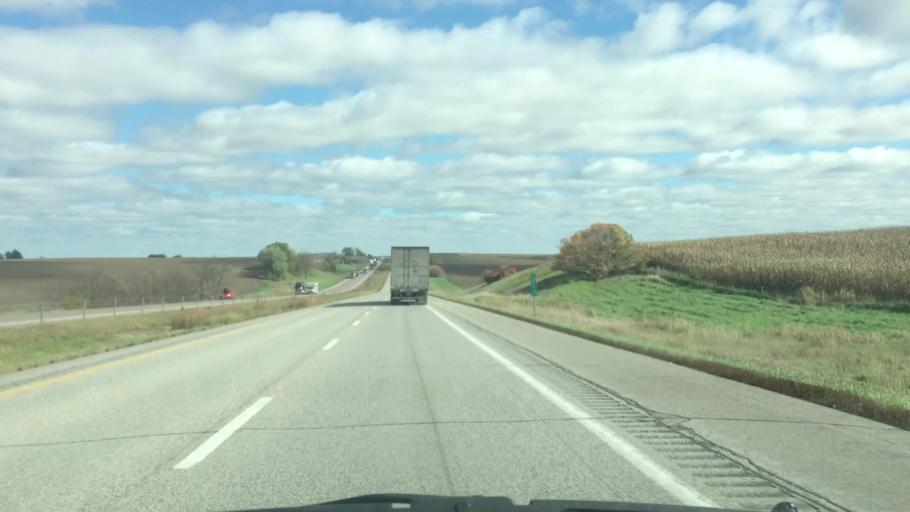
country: US
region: Iowa
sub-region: Iowa County
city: Marengo
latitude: 41.6955
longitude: -92.1428
